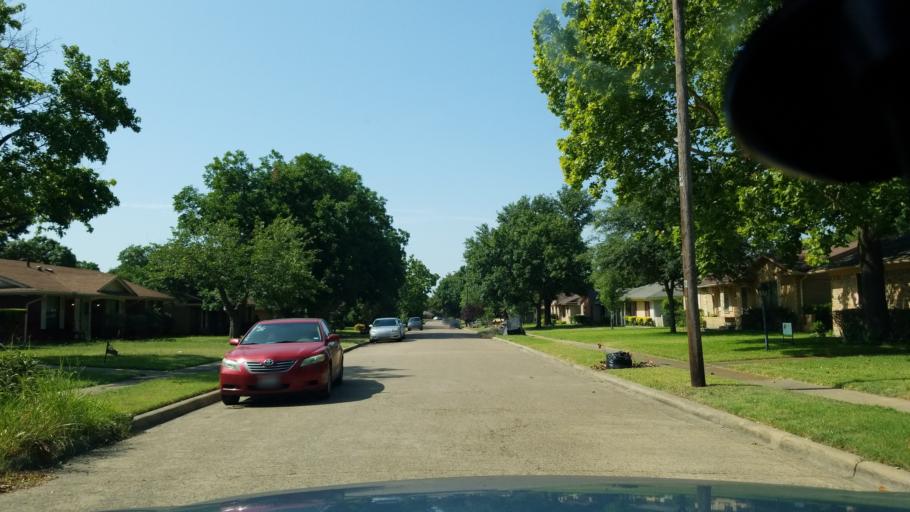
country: US
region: Texas
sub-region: Dallas County
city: Cockrell Hill
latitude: 32.6821
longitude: -96.8491
